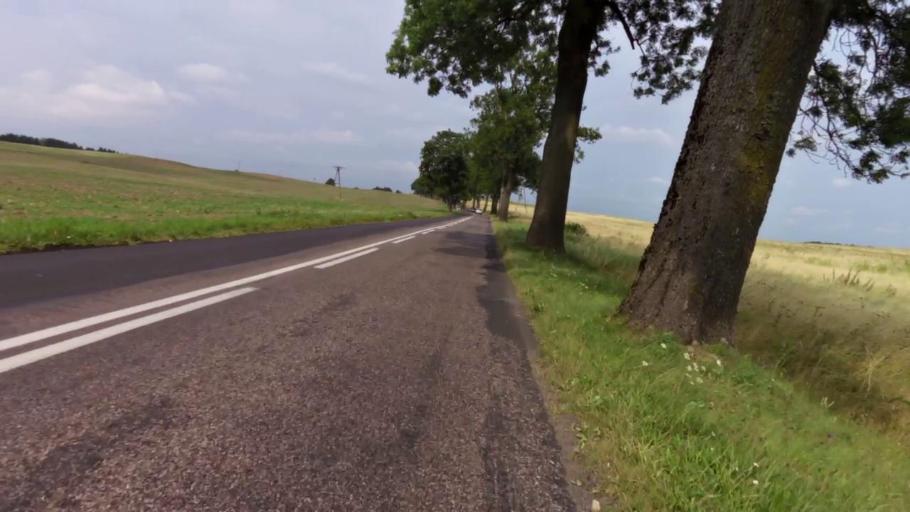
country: PL
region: West Pomeranian Voivodeship
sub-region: Powiat drawski
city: Drawsko Pomorskie
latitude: 53.5559
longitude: 15.8263
